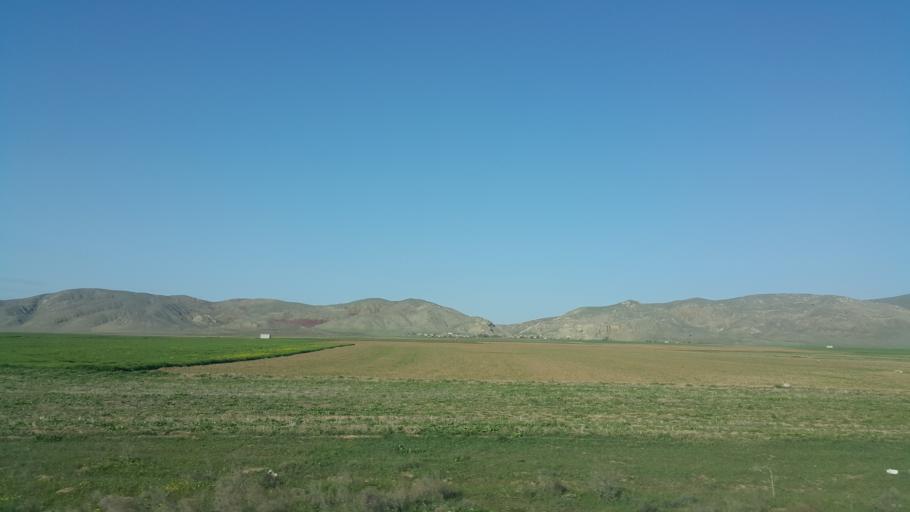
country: TR
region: Aksaray
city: Acipinar
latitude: 38.6391
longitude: 33.7363
